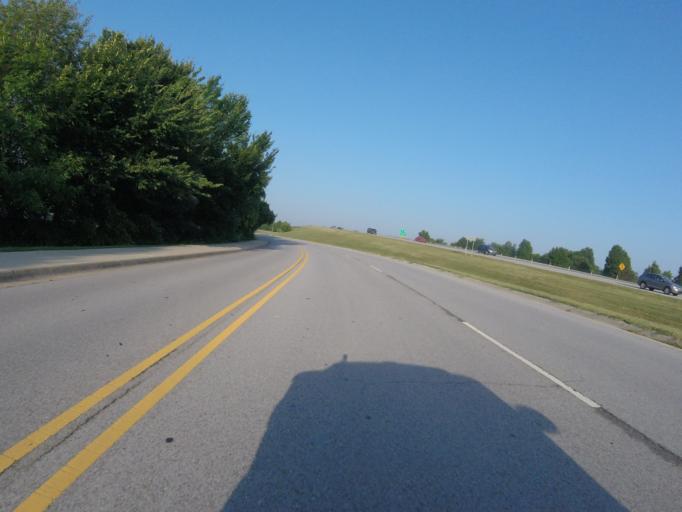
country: US
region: Arkansas
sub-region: Washington County
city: Johnson
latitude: 36.1119
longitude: -94.1606
